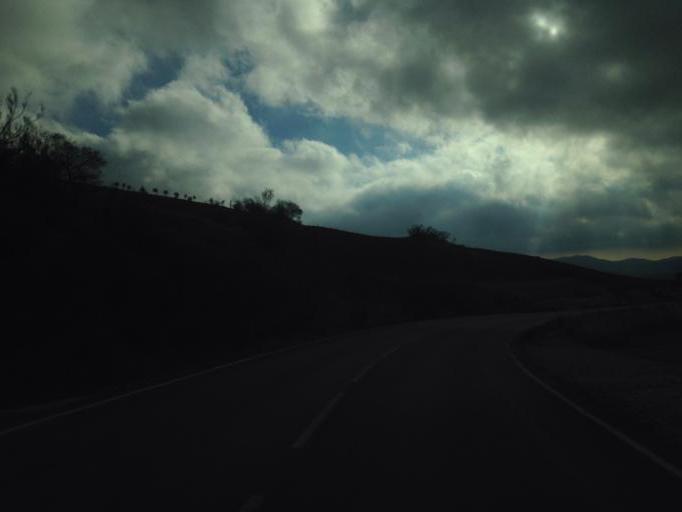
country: ES
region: Andalusia
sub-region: Provincia de Malaga
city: Casabermeja
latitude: 36.9357
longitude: -4.3896
